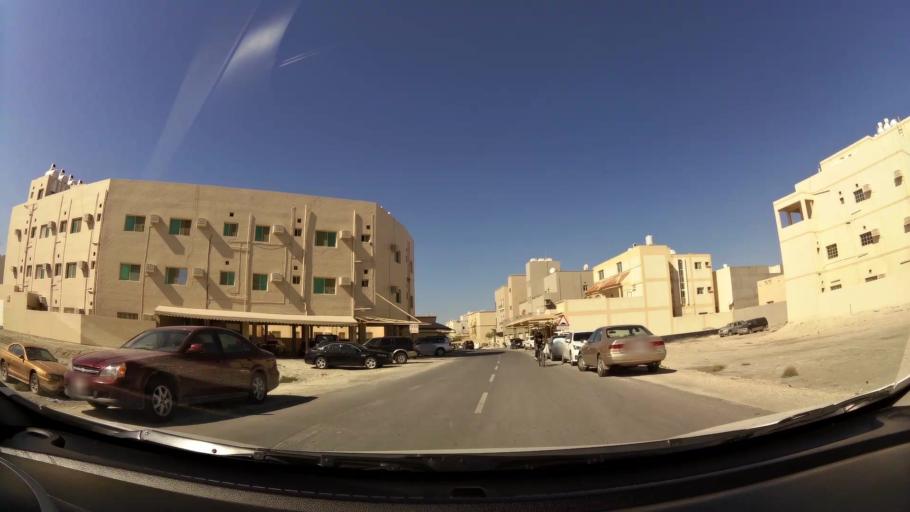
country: BH
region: Muharraq
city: Al Hadd
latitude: 26.2473
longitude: 50.6476
